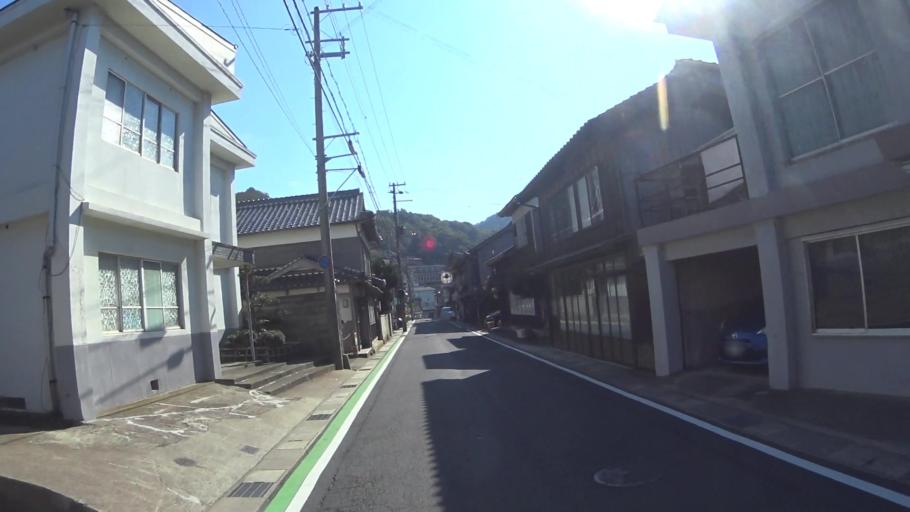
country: JP
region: Kyoto
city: Miyazu
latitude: 35.7382
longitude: 135.0942
